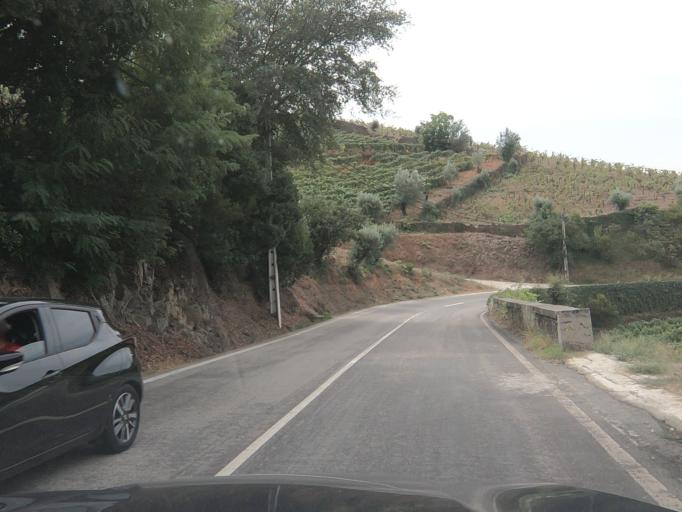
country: PT
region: Vila Real
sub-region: Santa Marta de Penaguiao
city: Santa Marta de Penaguiao
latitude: 41.2314
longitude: -7.7646
